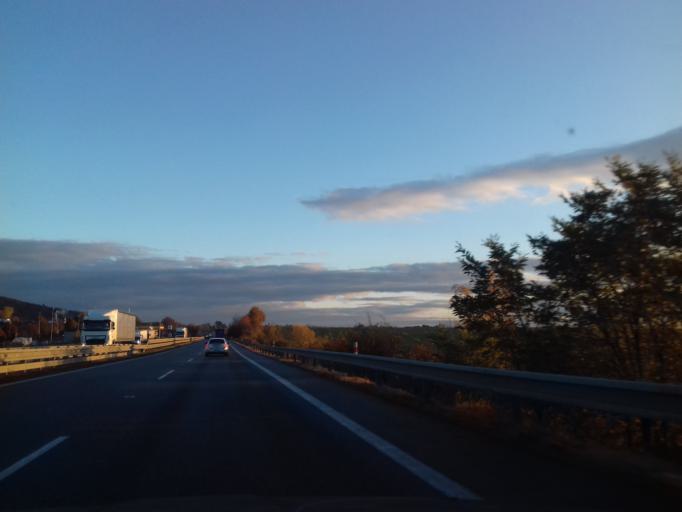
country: CZ
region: South Moravian
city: Pustimer
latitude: 49.3159
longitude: 17.0365
